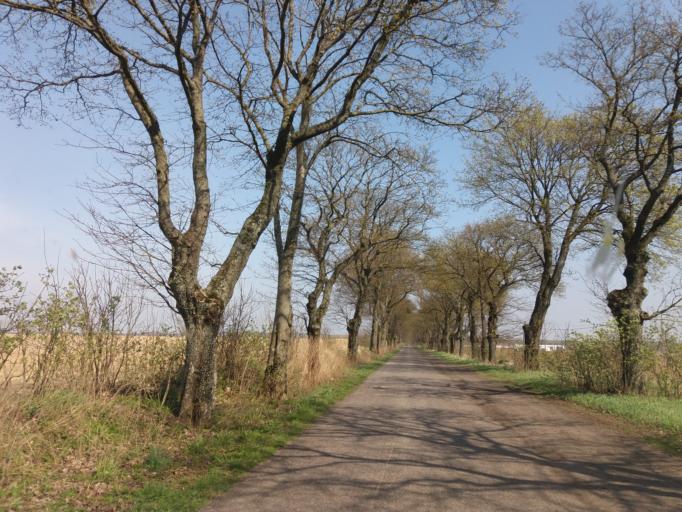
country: PL
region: West Pomeranian Voivodeship
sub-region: Powiat choszczenski
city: Recz
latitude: 53.2578
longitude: 15.6020
